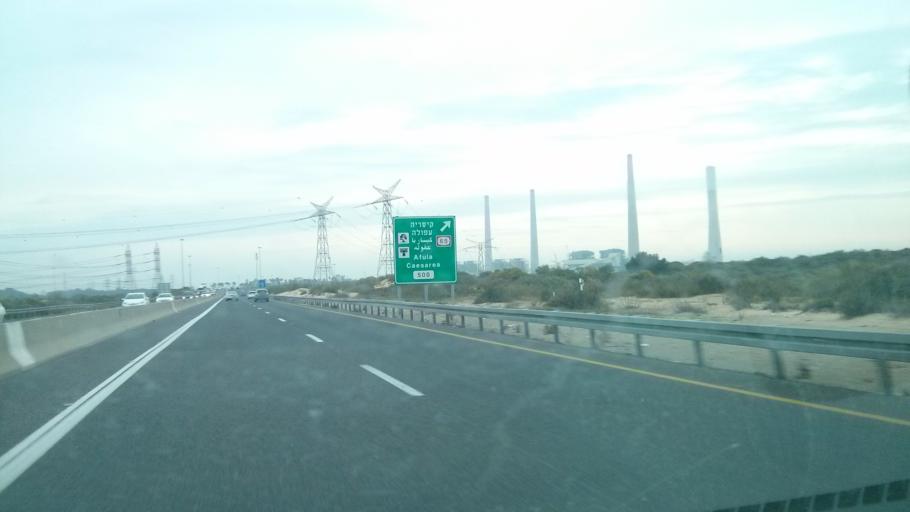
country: IL
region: Haifa
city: Hadera
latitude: 32.4786
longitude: 34.9065
